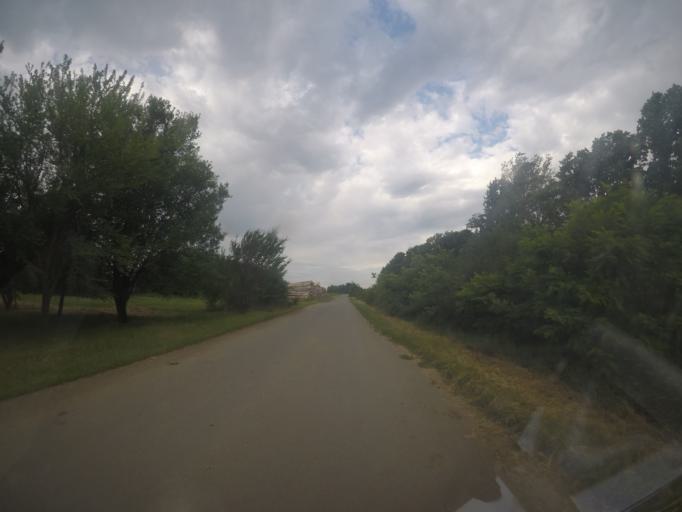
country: RS
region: Central Serbia
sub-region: Belgrade
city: Zemun
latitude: 44.9031
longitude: 20.4214
